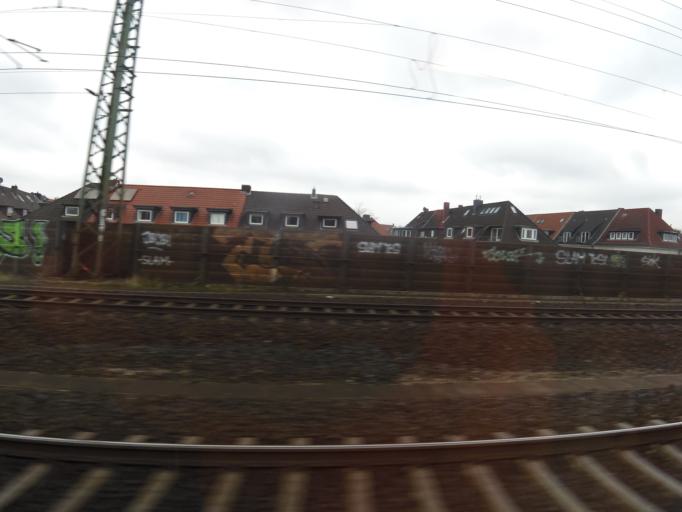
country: DE
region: Lower Saxony
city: Hannover
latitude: 52.3726
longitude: 9.7619
